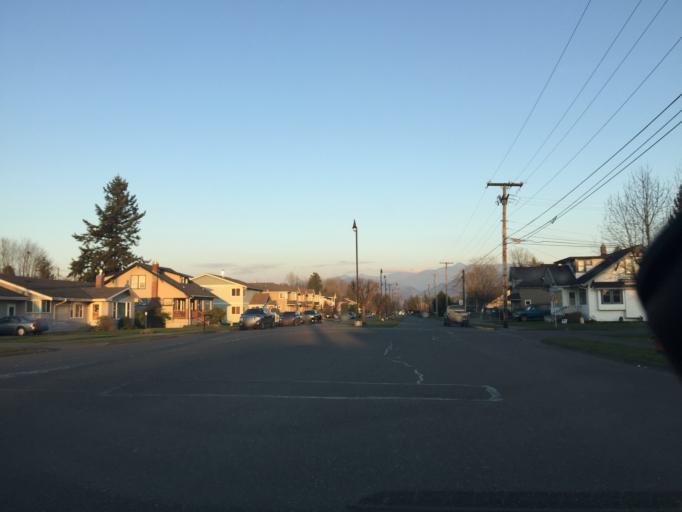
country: US
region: Washington
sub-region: Whatcom County
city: Sumas
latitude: 49.0000
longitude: -122.2635
